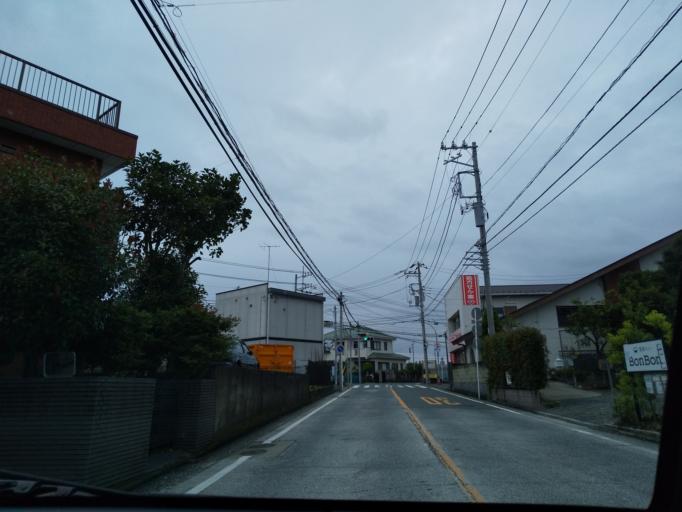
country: JP
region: Kanagawa
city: Fujisawa
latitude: 35.3925
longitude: 139.5062
